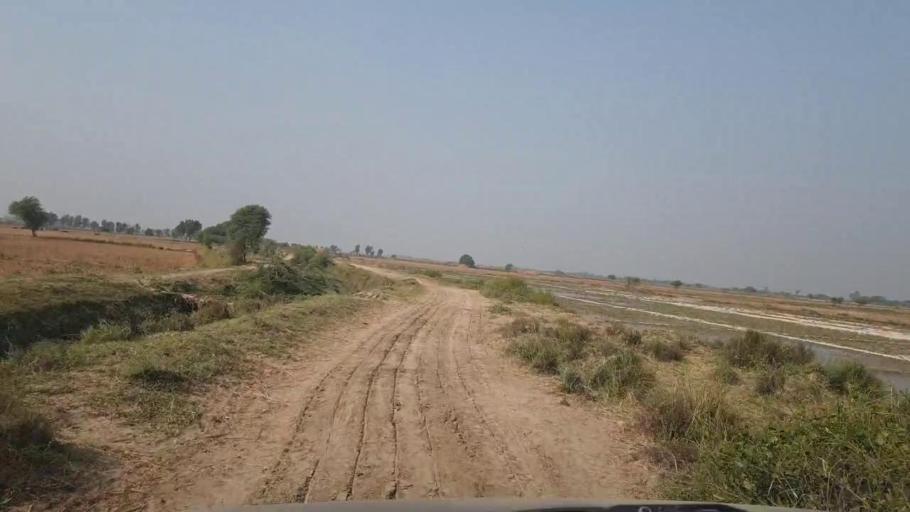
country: PK
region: Sindh
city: Tando Muhammad Khan
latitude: 25.0695
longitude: 68.3575
